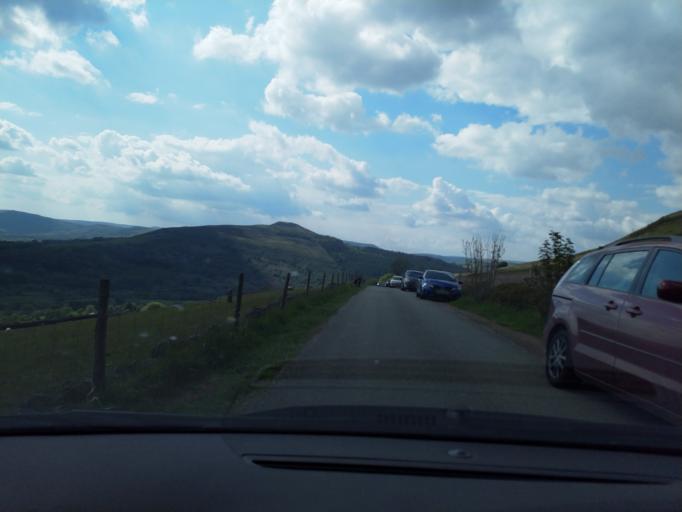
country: GB
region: England
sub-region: Derbyshire
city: Hathersage
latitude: 53.3527
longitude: -1.6814
